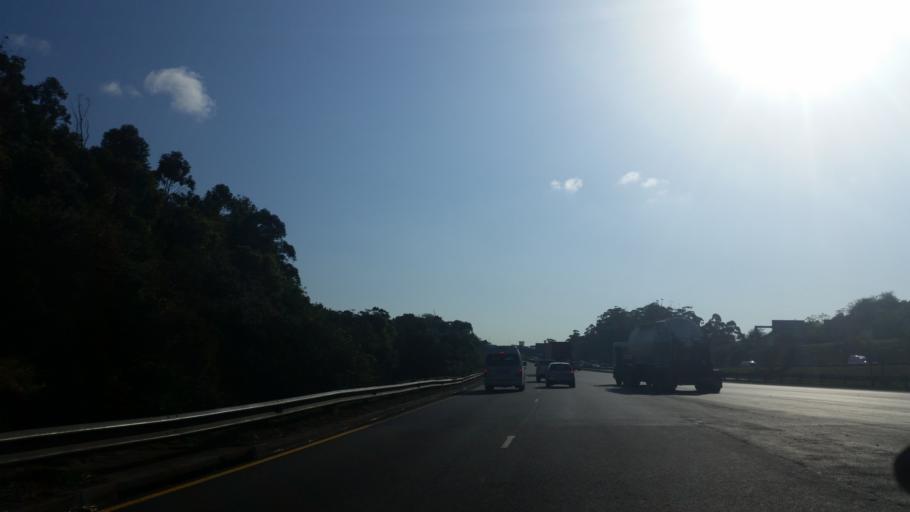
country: ZA
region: KwaZulu-Natal
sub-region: eThekwini Metropolitan Municipality
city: Berea
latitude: -29.8366
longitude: 30.9585
